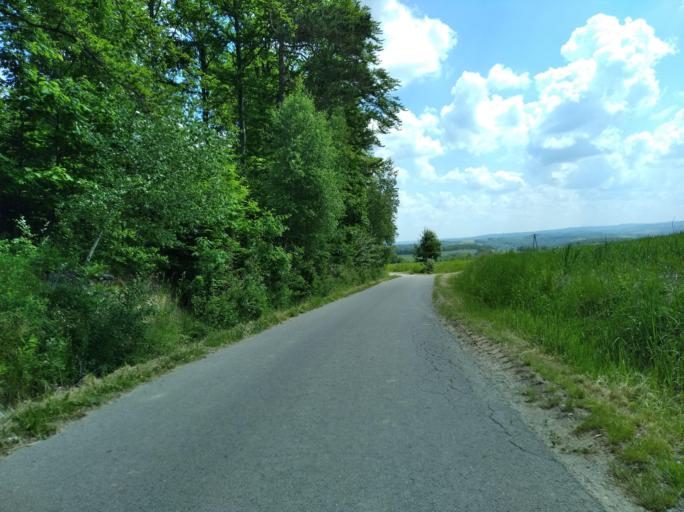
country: PL
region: Subcarpathian Voivodeship
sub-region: Powiat ropczycko-sedziszowski
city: Zagorzyce
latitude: 49.9651
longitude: 21.7052
